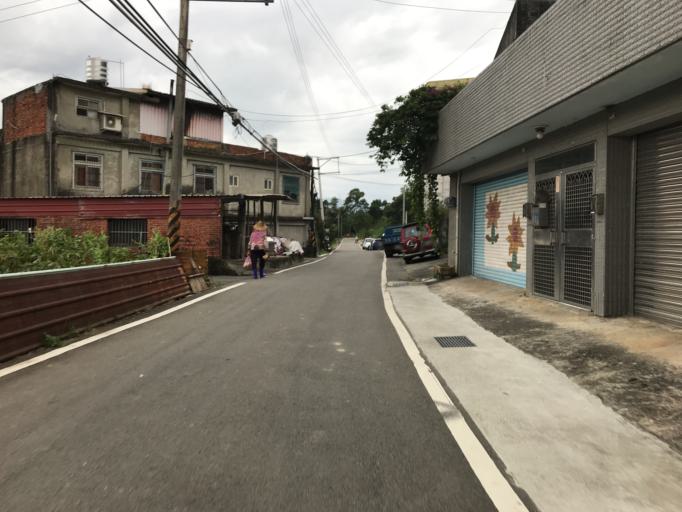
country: TW
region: Taiwan
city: Daxi
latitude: 24.7814
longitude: 121.1750
